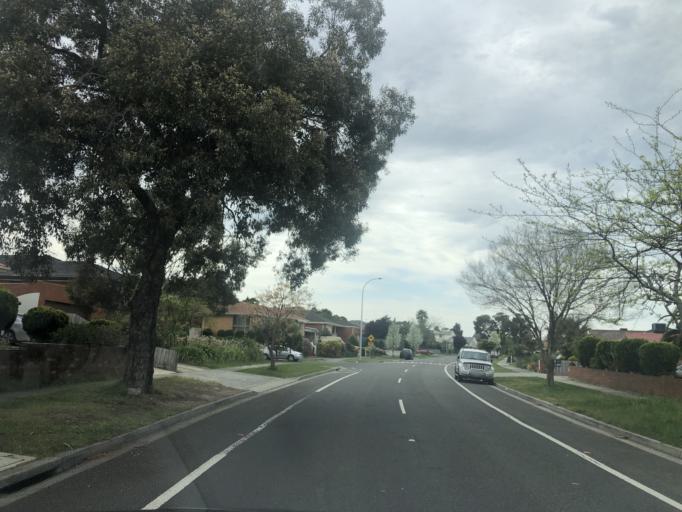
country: AU
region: Victoria
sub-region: Casey
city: Hallam
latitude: -38.0121
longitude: 145.2773
